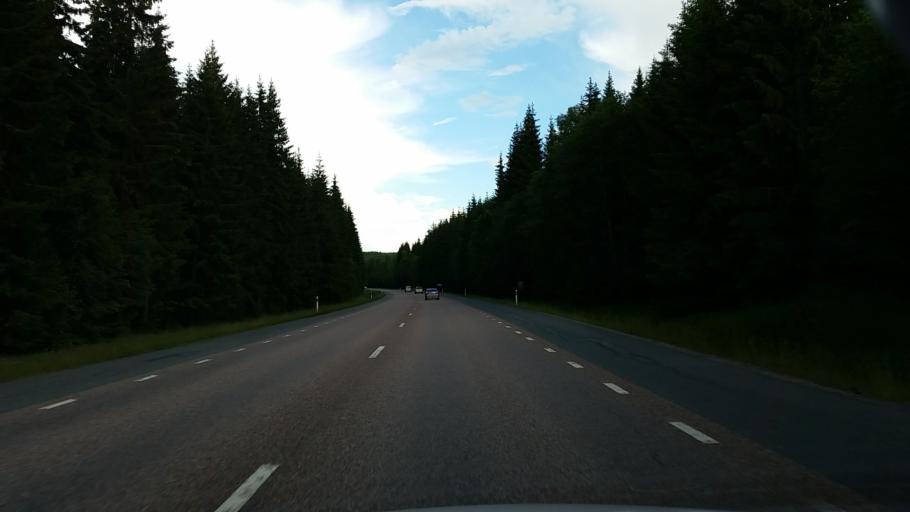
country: SE
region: Vaestmanland
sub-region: Fagersta Kommun
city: Fagersta
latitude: 59.9709
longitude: 15.7165
